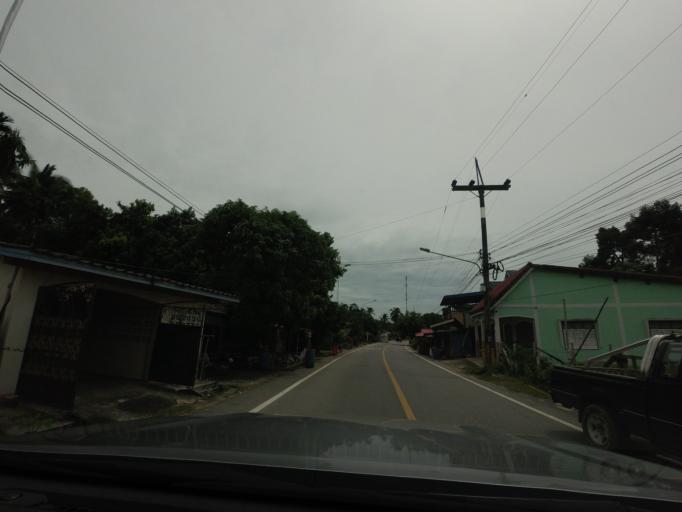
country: TH
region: Pattani
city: Kapho
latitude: 6.5941
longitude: 101.5304
